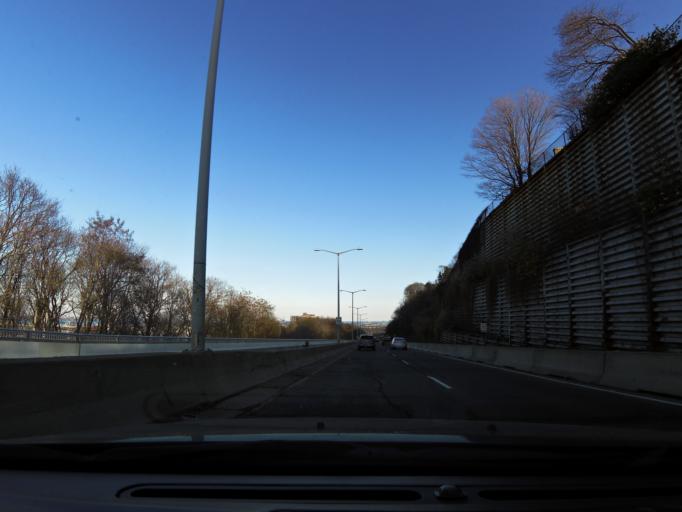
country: CA
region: Ontario
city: Hamilton
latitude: 43.2451
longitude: -79.8734
